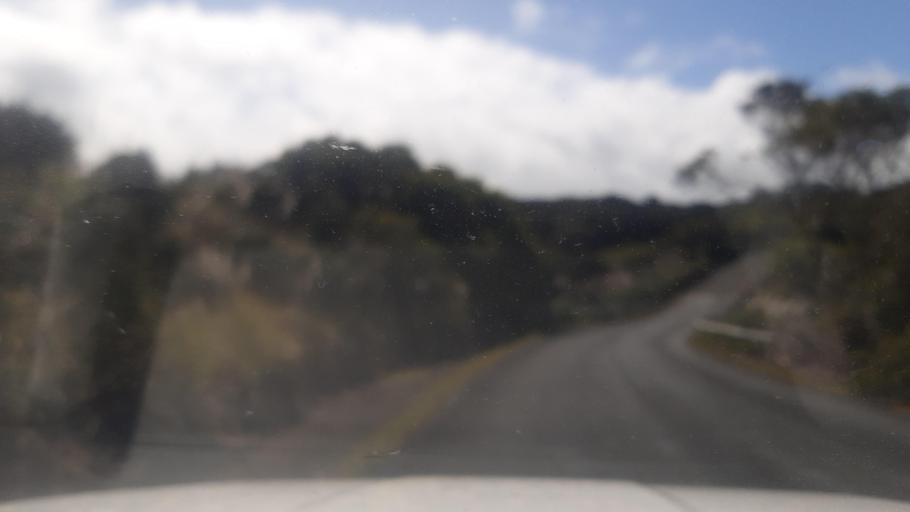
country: NZ
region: Northland
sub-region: Far North District
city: Kaitaia
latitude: -34.7413
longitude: 173.0960
